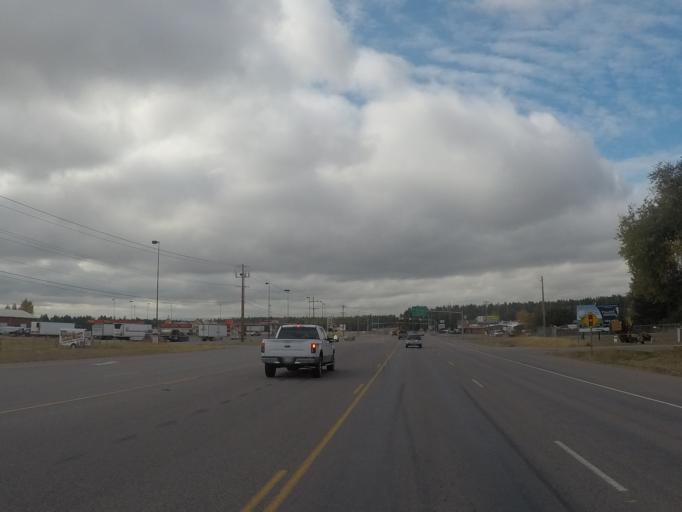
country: US
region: Montana
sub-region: Flathead County
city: Columbia Falls
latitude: 48.3708
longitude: -114.2363
